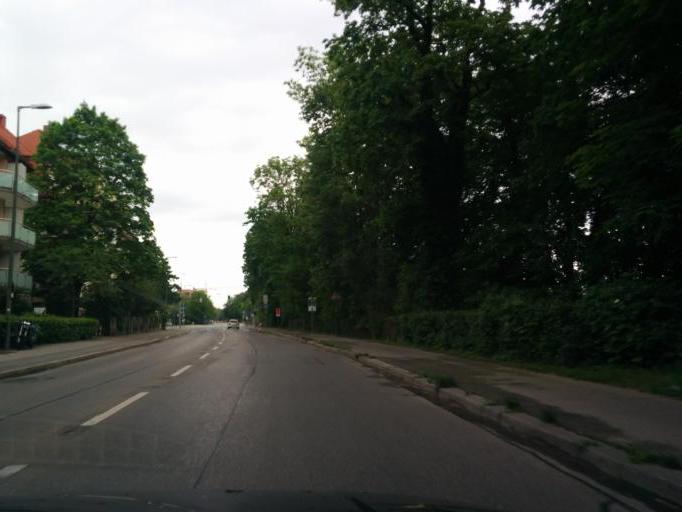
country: DE
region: Bavaria
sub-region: Upper Bavaria
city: Pullach im Isartal
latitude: 48.0996
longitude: 11.5415
